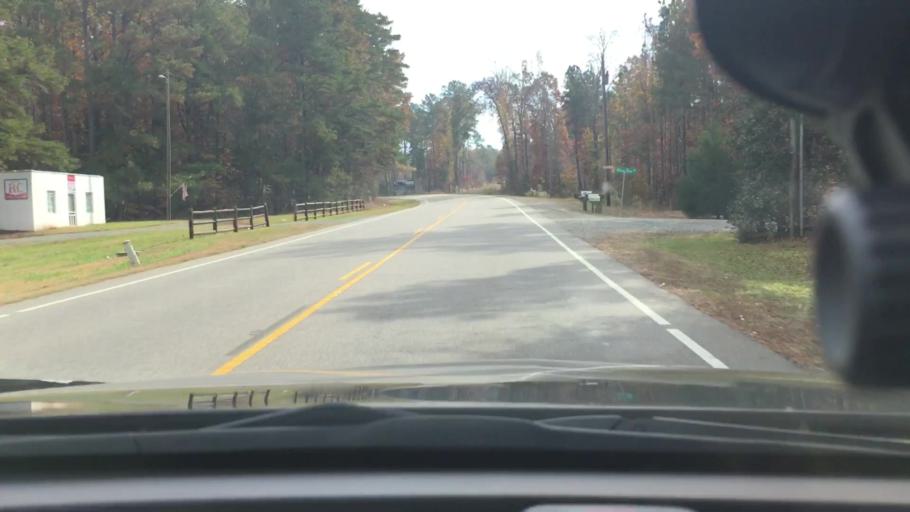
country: US
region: North Carolina
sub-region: Moore County
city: Carthage
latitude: 35.3636
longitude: -79.4426
